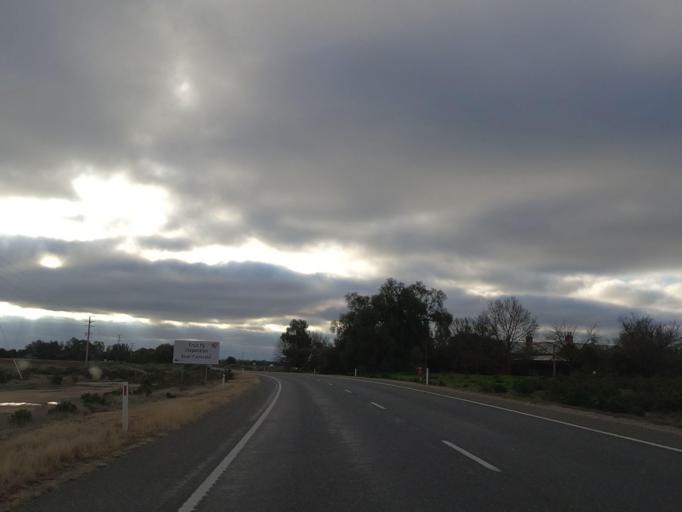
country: AU
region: Victoria
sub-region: Swan Hill
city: Swan Hill
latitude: -35.7244
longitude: 143.8898
